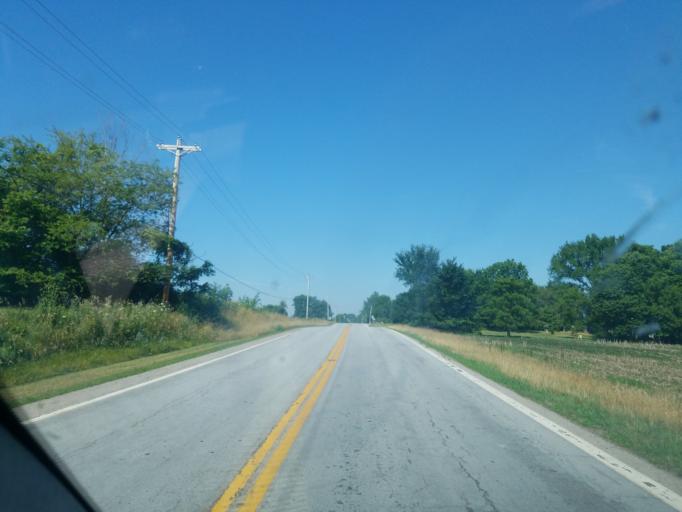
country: US
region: Ohio
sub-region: Logan County
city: Northwood
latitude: 40.4378
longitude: -83.7976
